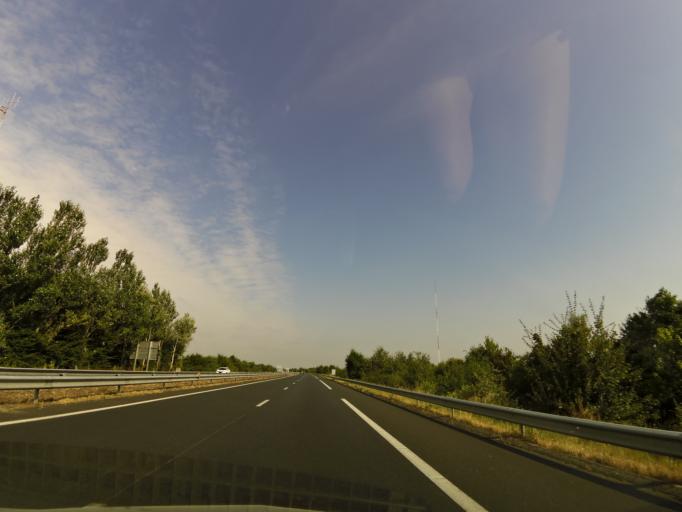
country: FR
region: Pays de la Loire
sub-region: Departement de la Vendee
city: Chauche
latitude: 46.8281
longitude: -1.2227
